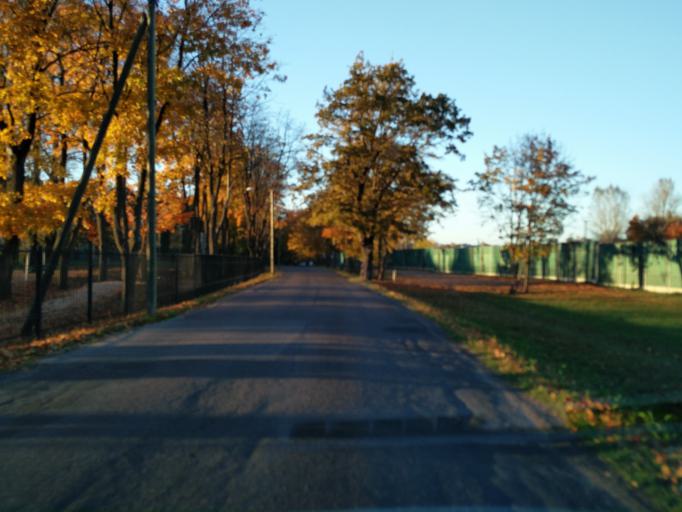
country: EE
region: Tartu
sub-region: Tartu linn
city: Tartu
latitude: 58.3665
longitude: 26.7157
